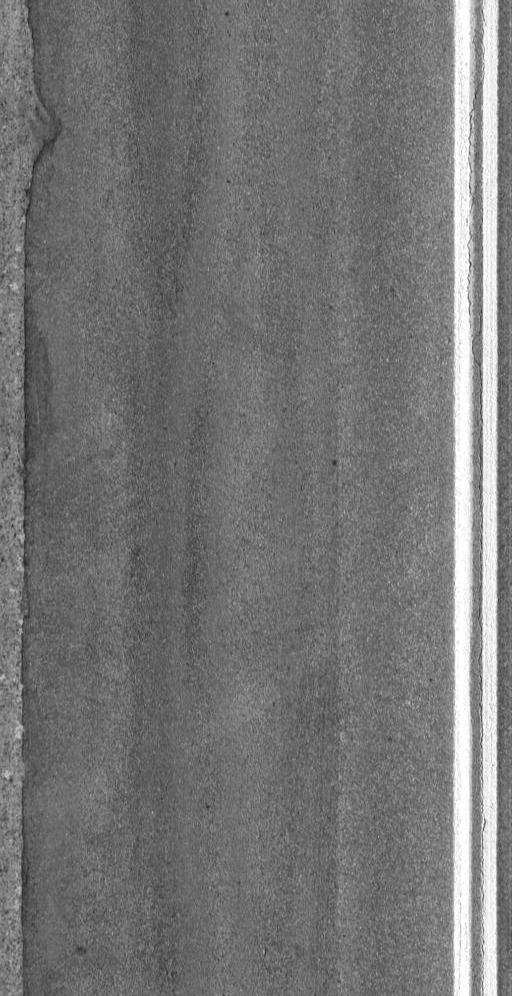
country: US
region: Vermont
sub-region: Rutland County
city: Rutland
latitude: 43.5663
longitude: -72.9457
